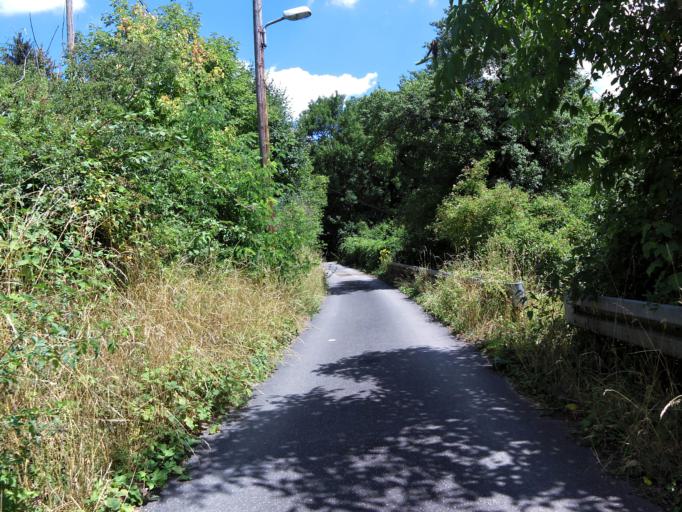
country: DE
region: Bavaria
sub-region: Regierungsbezirk Unterfranken
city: Hochberg
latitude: 49.7732
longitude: 9.9035
